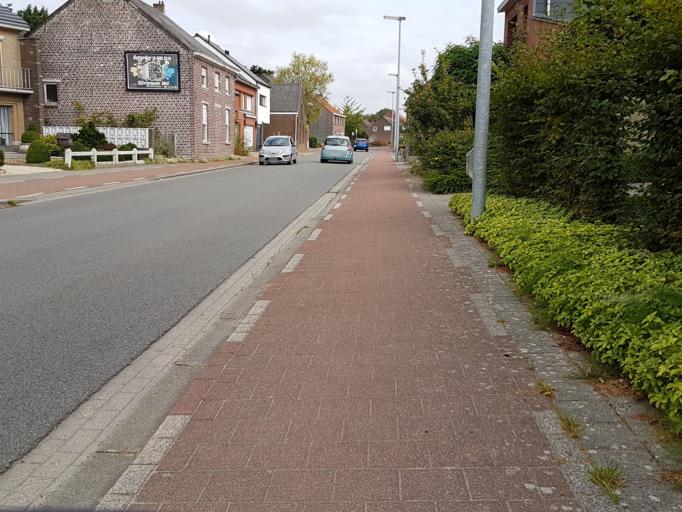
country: BE
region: Flanders
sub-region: Provincie Vlaams-Brabant
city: Haacht
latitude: 50.9606
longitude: 4.6251
